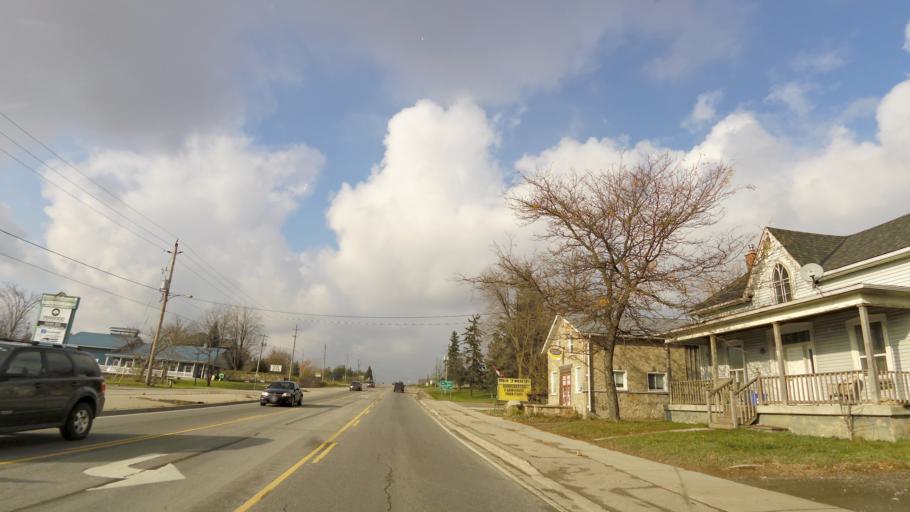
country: CA
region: Ontario
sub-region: Wellington County
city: Guelph
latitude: 43.4485
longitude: -80.1176
